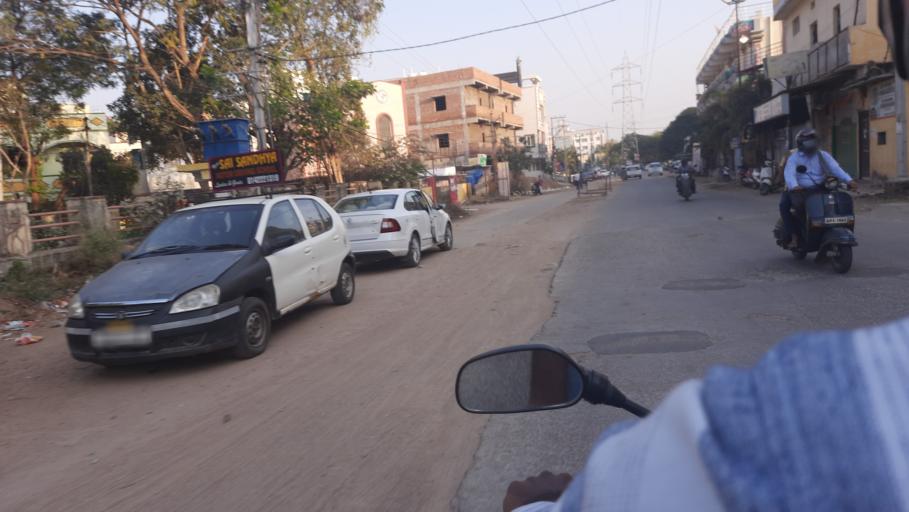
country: IN
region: Telangana
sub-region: Rangareddi
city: Secunderabad
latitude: 17.4978
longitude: 78.5422
